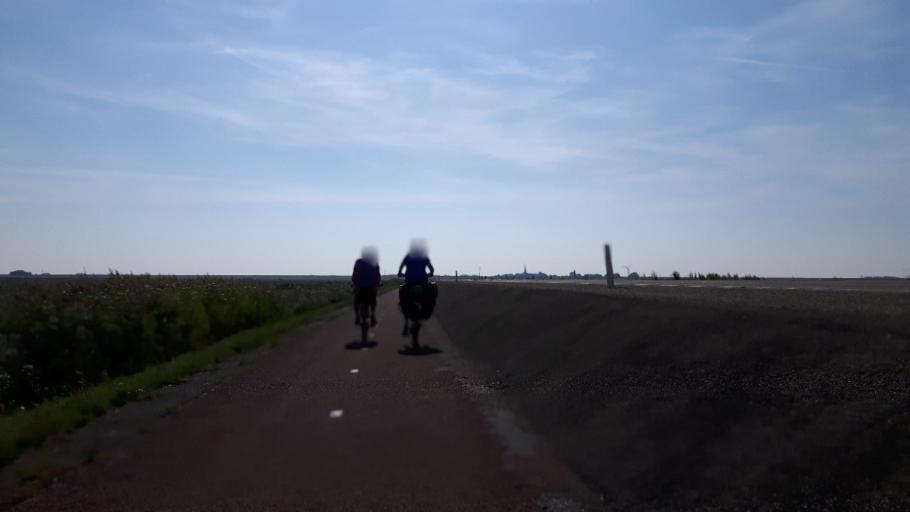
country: NL
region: Friesland
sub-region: Gemeente Dongeradeel
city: Holwerd
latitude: 53.3893
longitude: 5.8853
